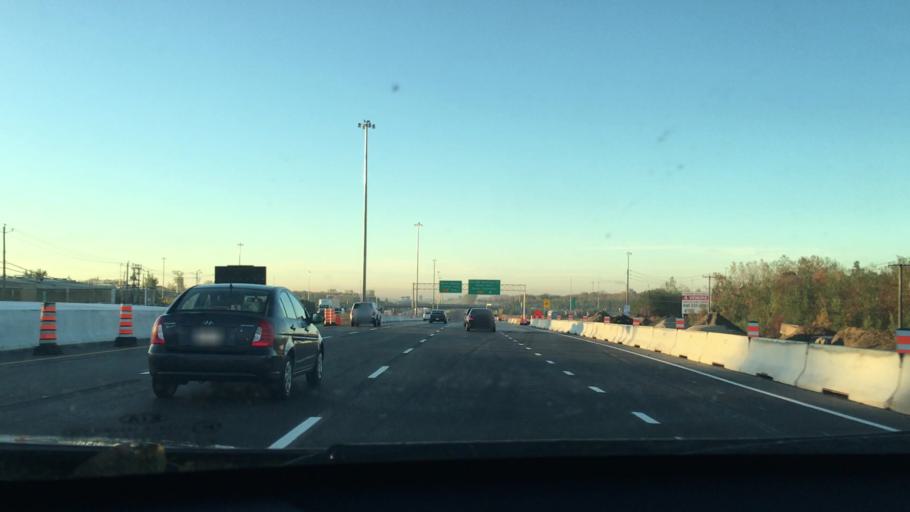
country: CA
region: Quebec
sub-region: Laurentides
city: Saint-Jerome
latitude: 45.7851
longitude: -74.0208
